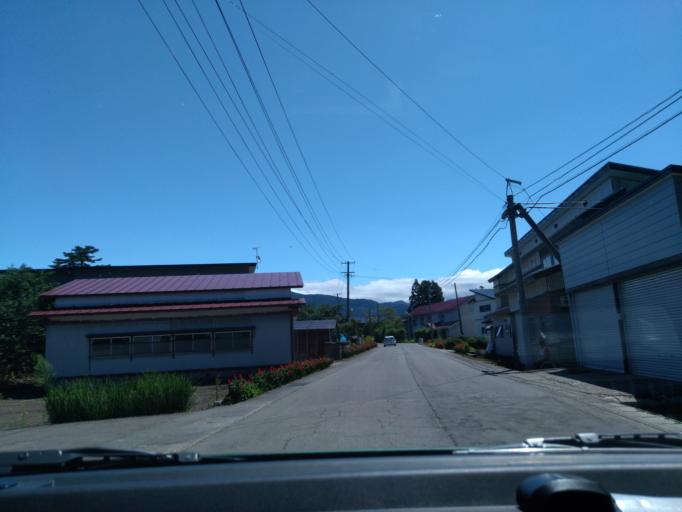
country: JP
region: Akita
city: Kakunodatemachi
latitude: 39.5286
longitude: 140.6051
